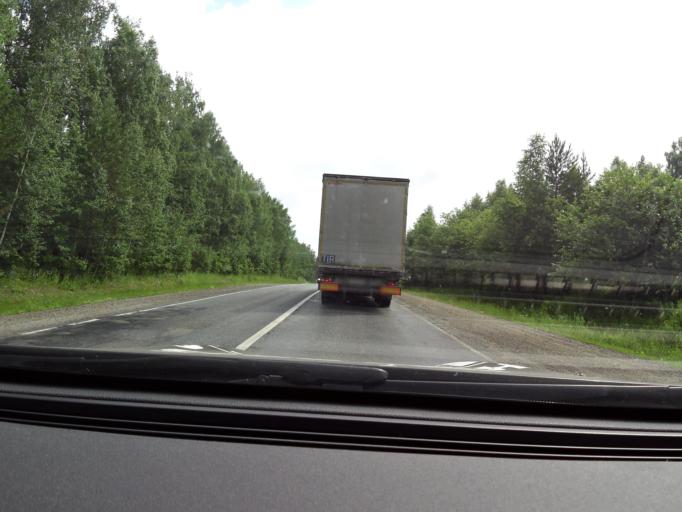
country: RU
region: Perm
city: Suksun
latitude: 57.0894
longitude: 57.3946
